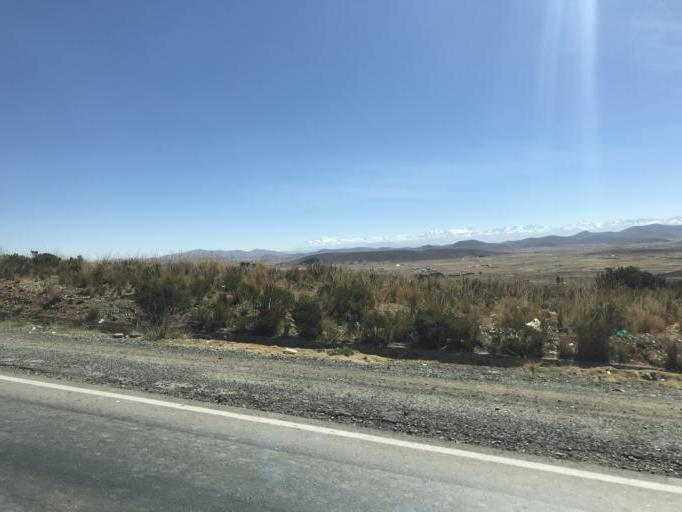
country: BO
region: La Paz
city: Tiahuanaco
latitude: -16.5828
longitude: -68.5212
